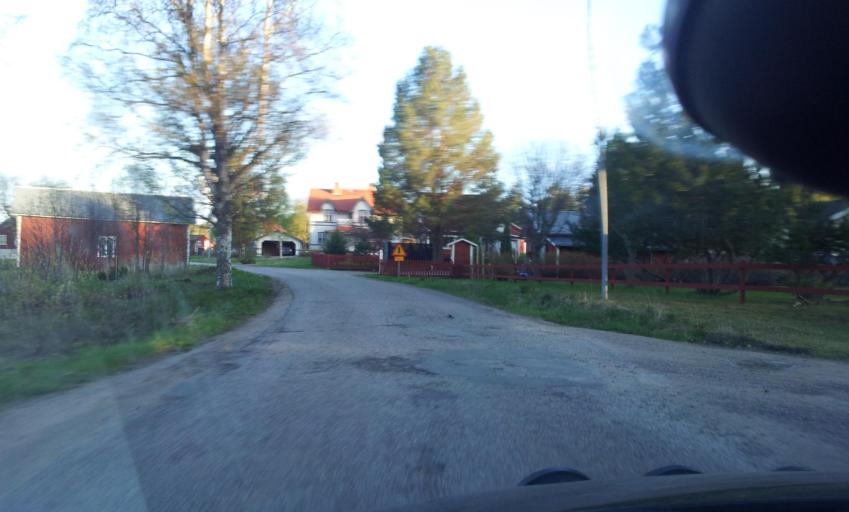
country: SE
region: Gaevleborg
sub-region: Bollnas Kommun
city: Kilafors
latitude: 61.3944
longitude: 16.6104
